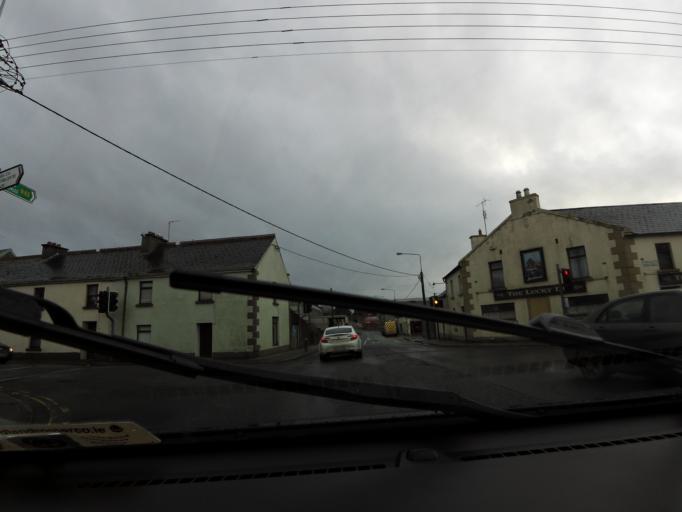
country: IE
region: Munster
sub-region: North Tipperary
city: Roscrea
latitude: 52.9578
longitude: -7.7977
